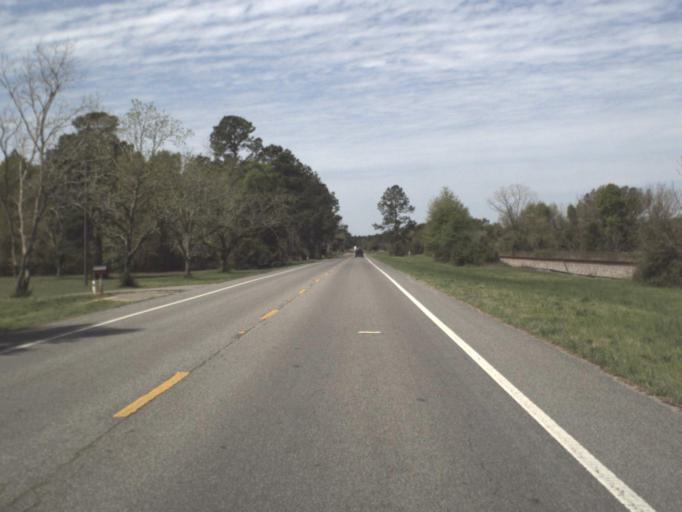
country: US
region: Florida
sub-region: Okaloosa County
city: Crestview
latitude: 30.7241
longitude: -86.7118
